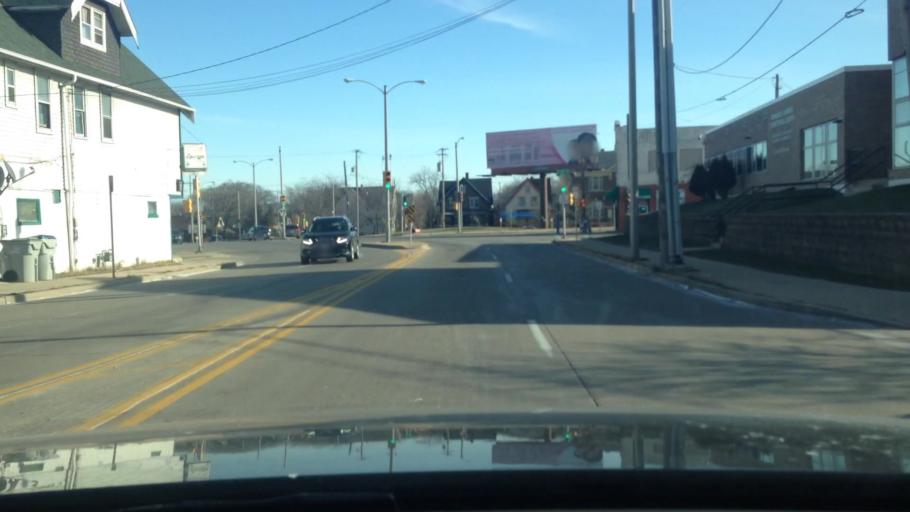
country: US
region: Wisconsin
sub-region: Milwaukee County
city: Shorewood
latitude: 43.0816
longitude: -87.9194
